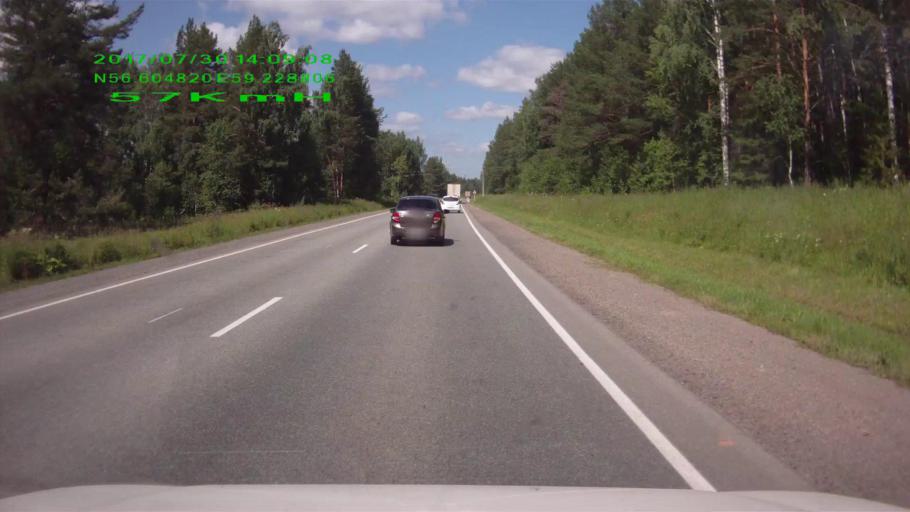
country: RU
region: Sverdlovsk
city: Nizhniye Sergi
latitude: 56.6050
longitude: 59.2288
